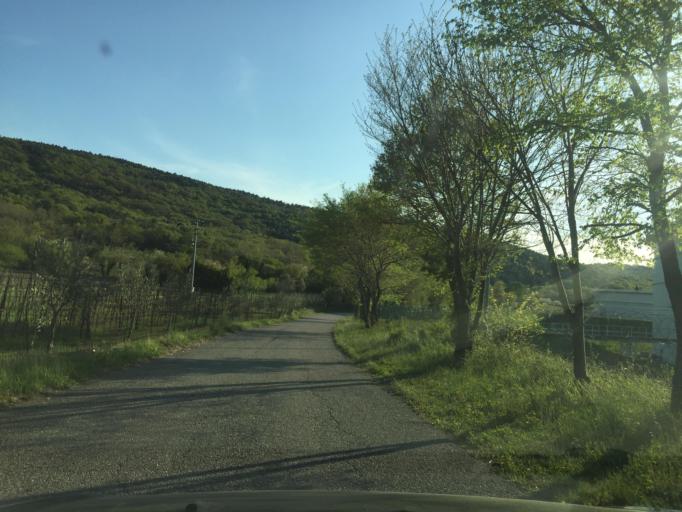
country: IT
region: Friuli Venezia Giulia
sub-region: Provincia di Trieste
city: Dolina
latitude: 45.5993
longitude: 13.8498
